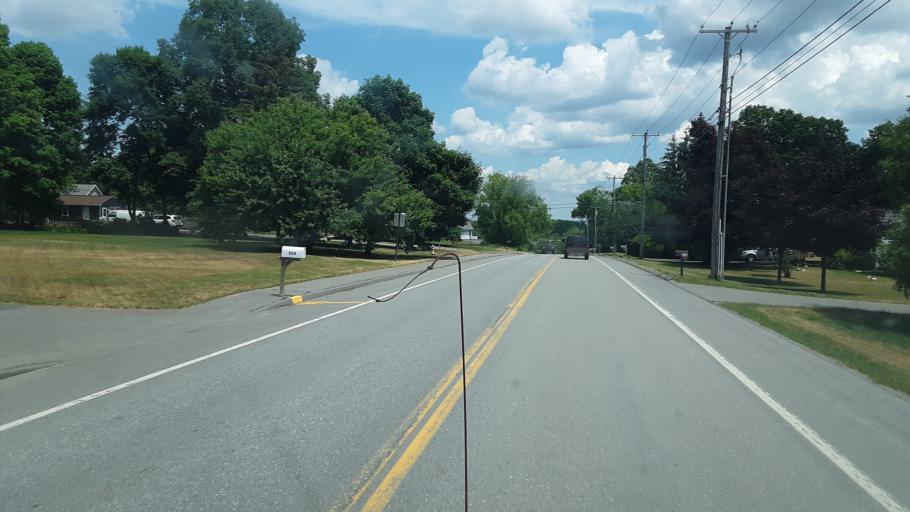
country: US
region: Maine
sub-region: Penobscot County
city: Hampden
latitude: 44.7641
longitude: -68.8042
